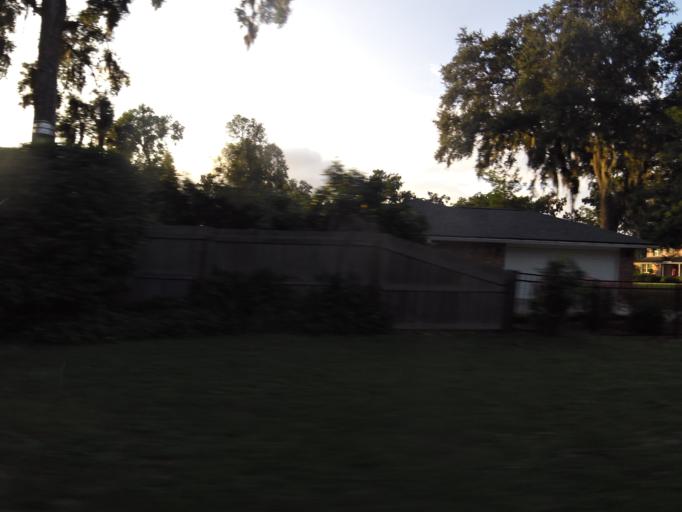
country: US
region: Florida
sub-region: Clay County
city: Orange Park
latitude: 30.2050
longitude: -81.6327
